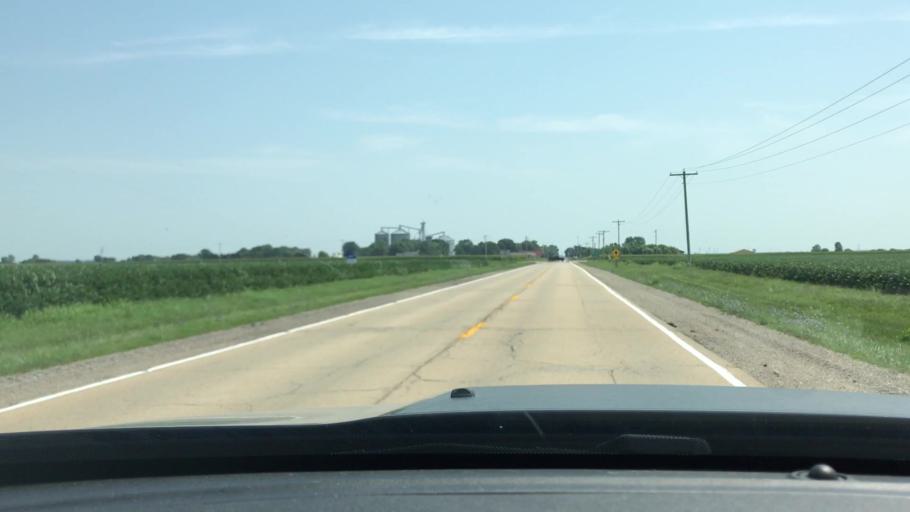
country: US
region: Illinois
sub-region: LaSalle County
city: Sheridan
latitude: 41.4851
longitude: -88.7449
